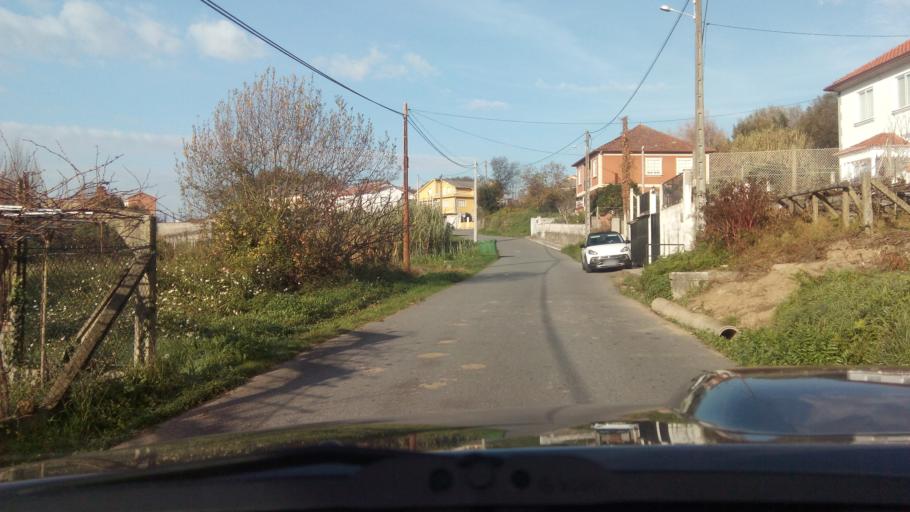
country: ES
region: Galicia
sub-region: Provincia de Pontevedra
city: Marin
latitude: 42.3670
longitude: -8.7262
